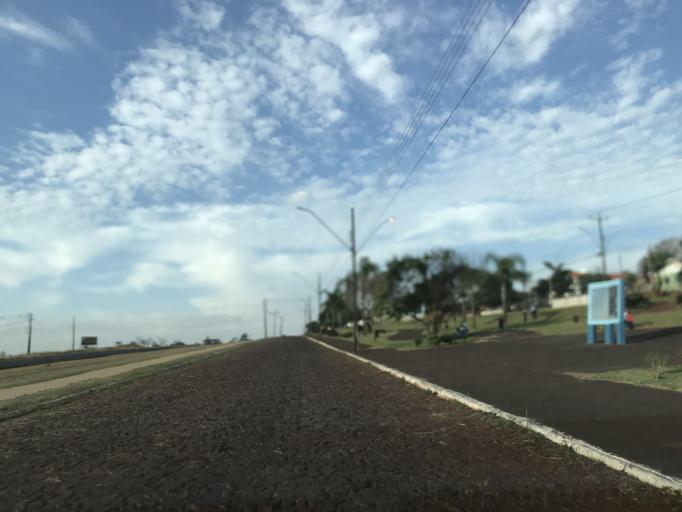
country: BR
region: Parana
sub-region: Cascavel
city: Cascavel
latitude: -25.0480
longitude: -53.6128
